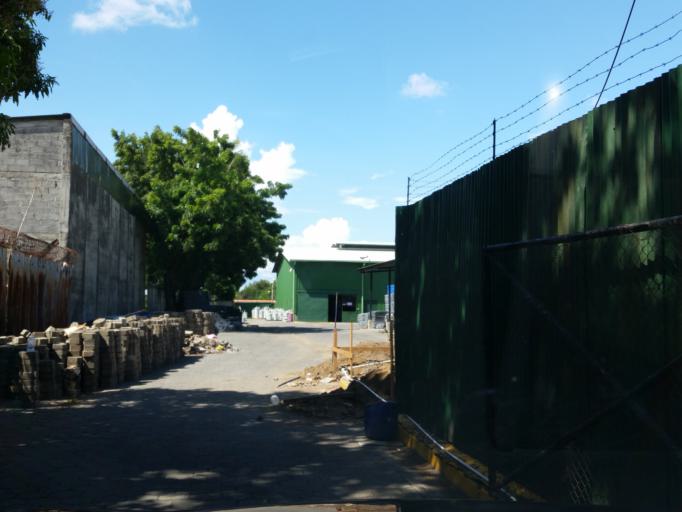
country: NI
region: Managua
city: Managua
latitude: 12.1490
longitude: -86.1988
